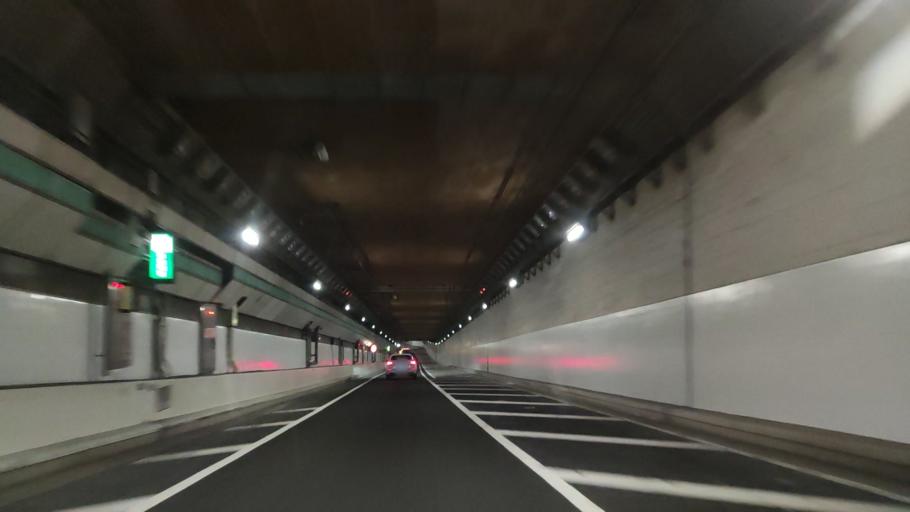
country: JP
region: Kanagawa
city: Yokohama
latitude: 35.4401
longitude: 139.6431
